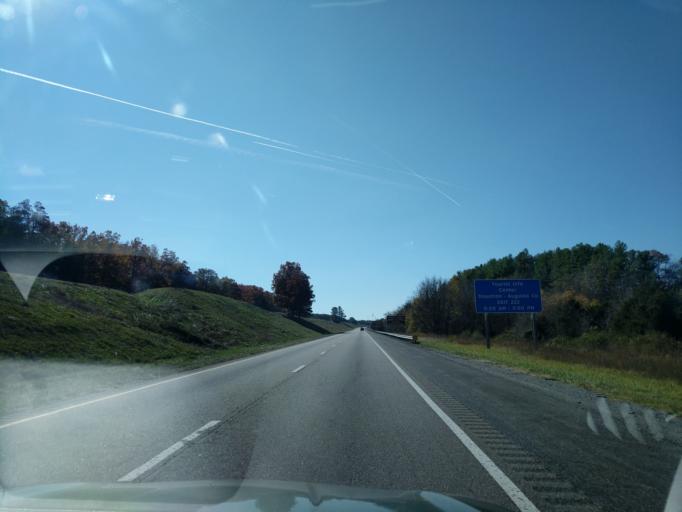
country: US
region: Virginia
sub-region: City of Staunton
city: Staunton
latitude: 38.1409
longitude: -79.0221
